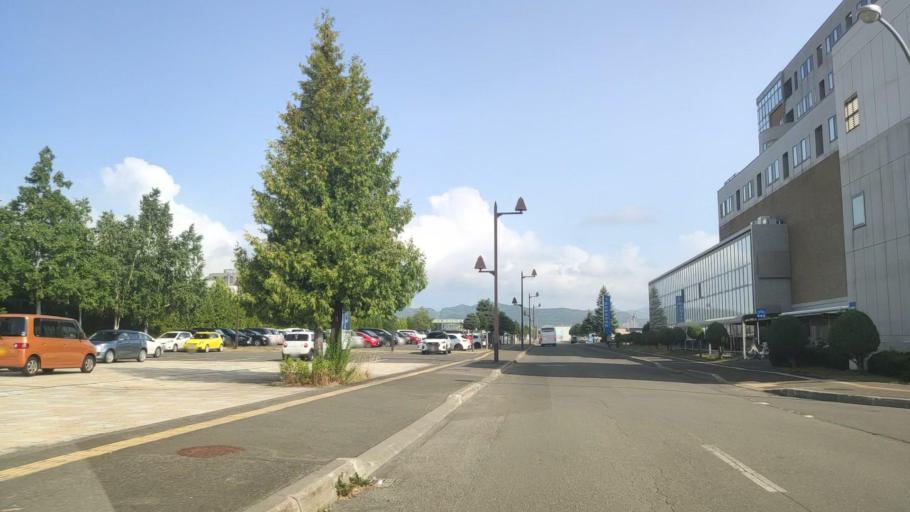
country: JP
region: Hokkaido
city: Shimo-furano
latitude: 43.3468
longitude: 142.3925
